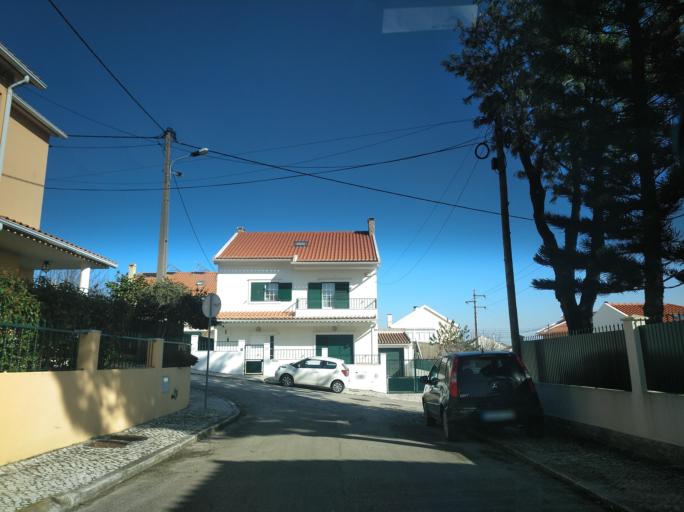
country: PT
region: Lisbon
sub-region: Odivelas
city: Famoes
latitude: 38.7992
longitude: -9.2158
